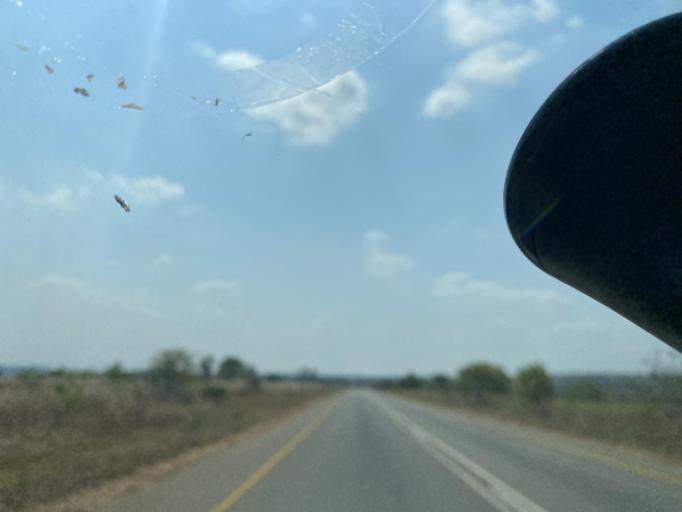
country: ZM
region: Lusaka
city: Chongwe
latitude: -15.5483
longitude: 28.6719
